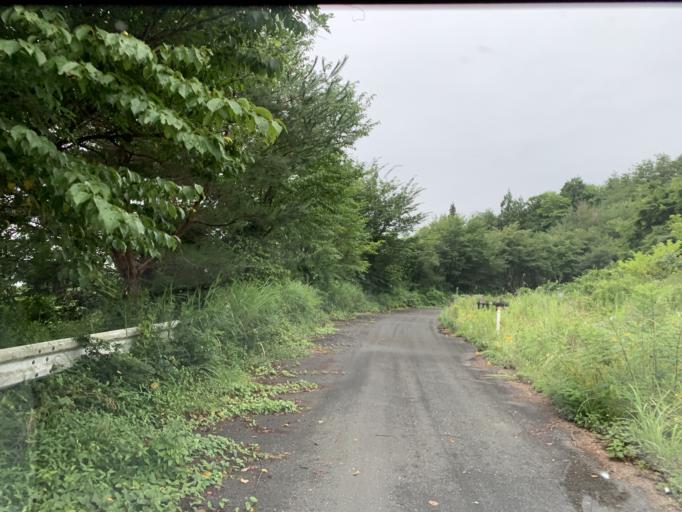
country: JP
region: Iwate
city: Ichinoseki
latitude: 38.8217
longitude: 141.2169
